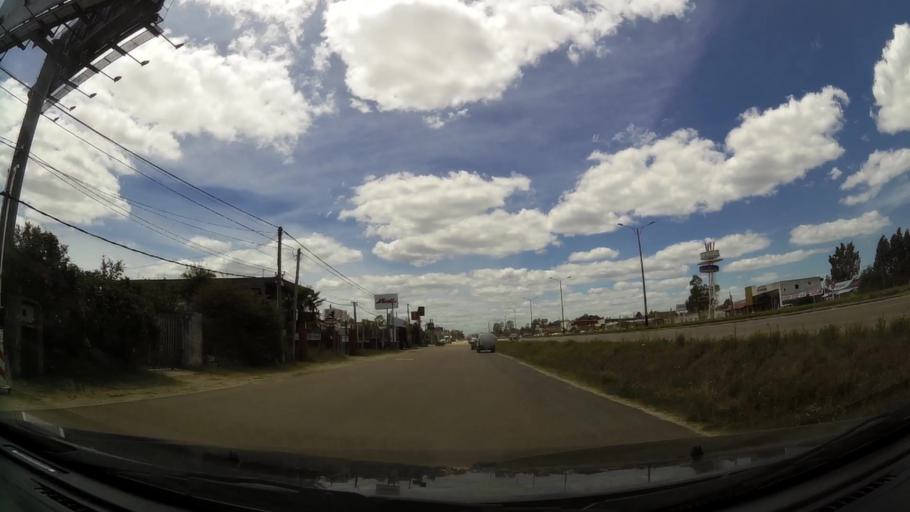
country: UY
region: Canelones
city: Colonia Nicolich
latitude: -34.8291
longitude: -55.9719
